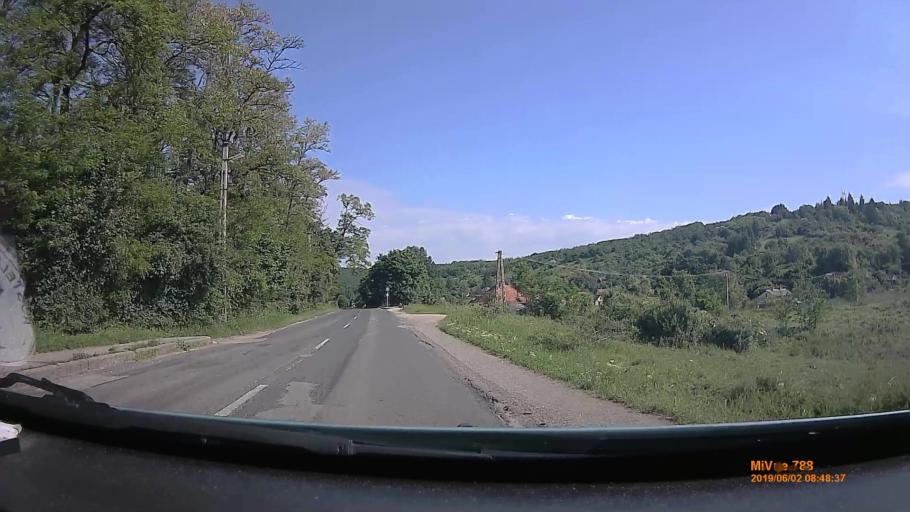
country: HU
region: Borsod-Abauj-Zemplen
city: Sajobabony
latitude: 48.1377
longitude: 20.7038
